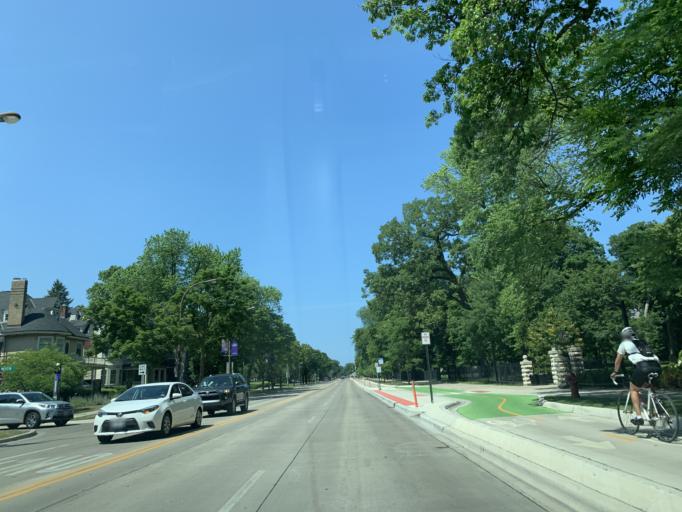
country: US
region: Illinois
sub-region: Cook County
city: Evanston
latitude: 42.0518
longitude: -87.6772
